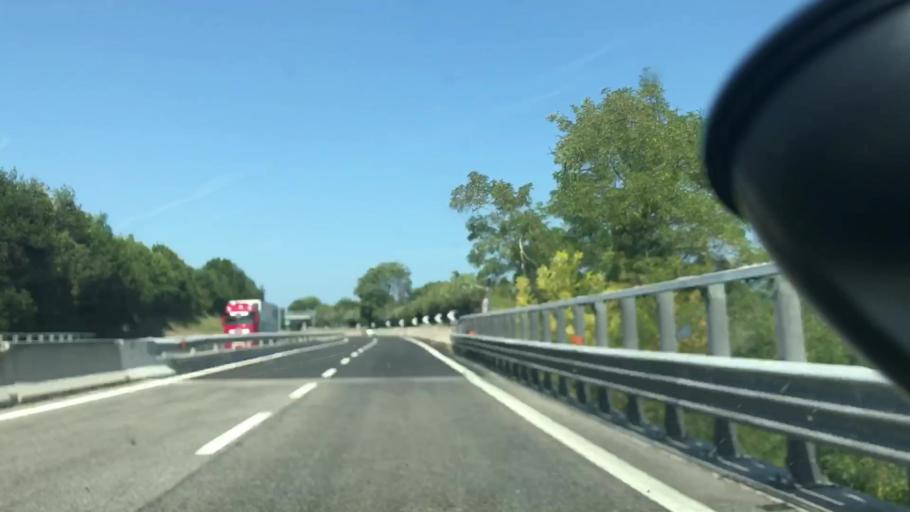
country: IT
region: Abruzzo
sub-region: Provincia di Chieti
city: Tollo
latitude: 42.3557
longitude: 14.3513
